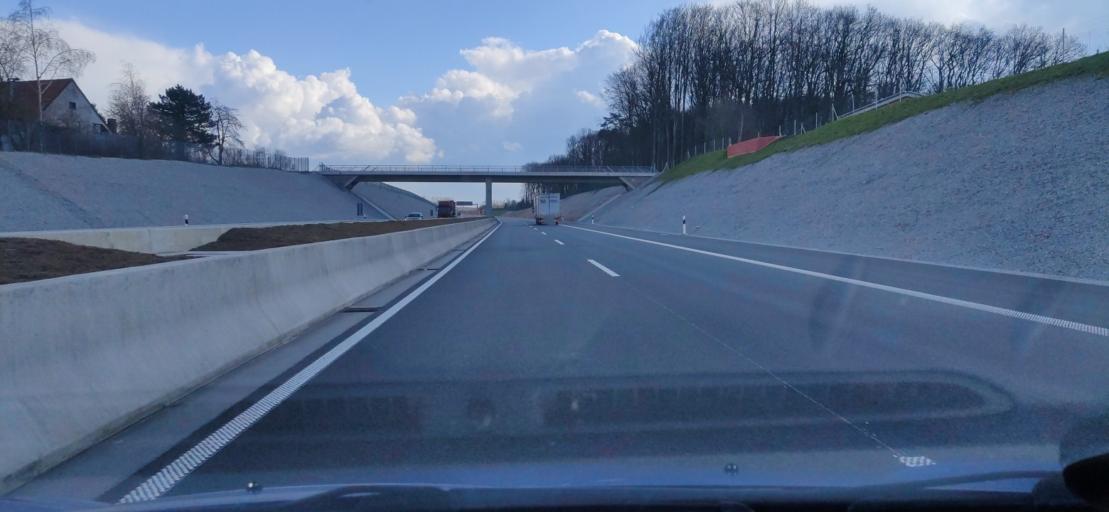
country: DE
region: North Rhine-Westphalia
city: Borgholzhausen
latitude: 52.0749
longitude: 8.2501
